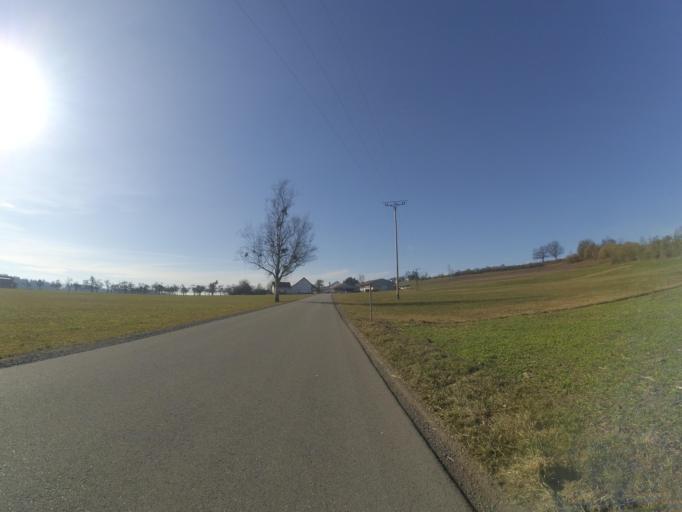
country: DE
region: Baden-Wuerttemberg
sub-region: Tuebingen Region
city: Wolpertswende
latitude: 47.9019
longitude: 9.6200
